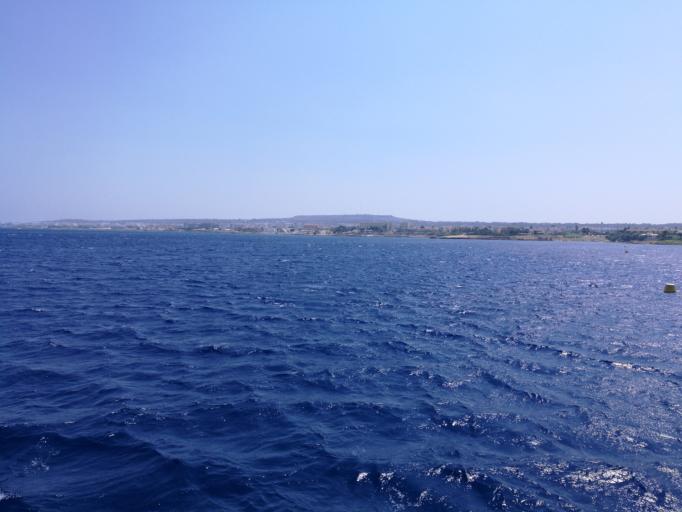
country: CY
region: Ammochostos
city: Protaras
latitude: 35.0475
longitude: 34.0394
